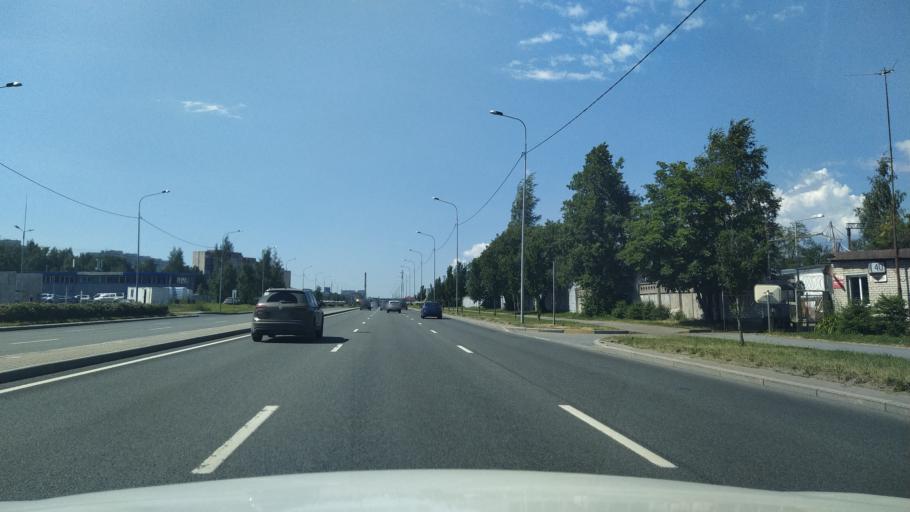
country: RU
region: Leningrad
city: Bugry
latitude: 60.0538
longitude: 30.3746
